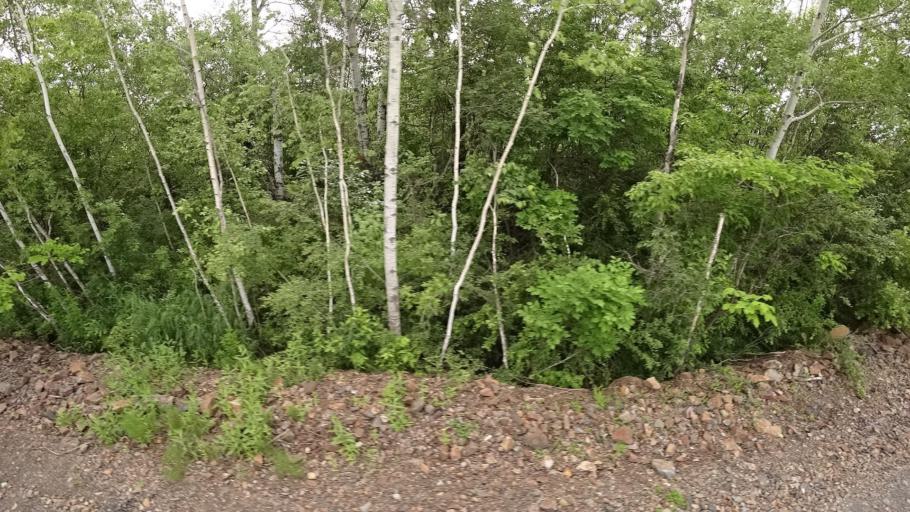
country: RU
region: Khabarovsk Krai
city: Amursk
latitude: 49.8969
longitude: 136.1463
